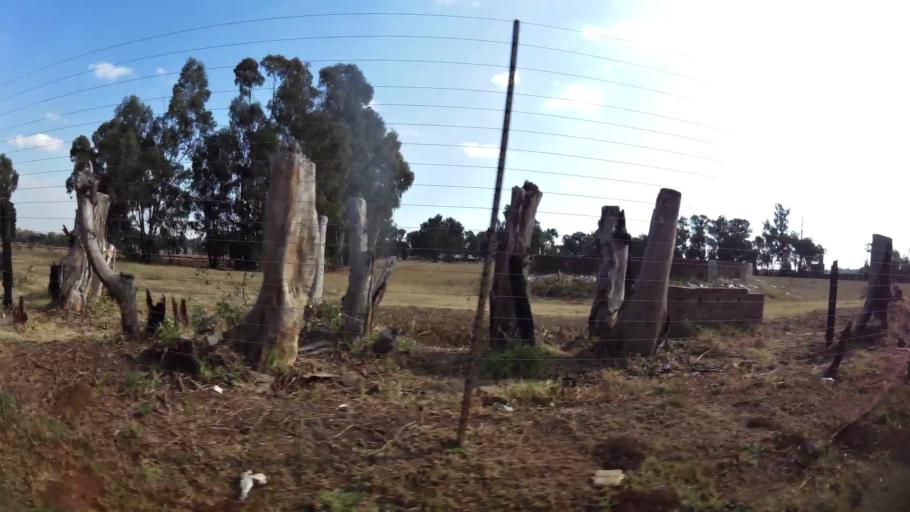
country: ZA
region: Gauteng
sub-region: Ekurhuleni Metropolitan Municipality
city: Benoni
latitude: -26.0901
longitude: 28.3641
